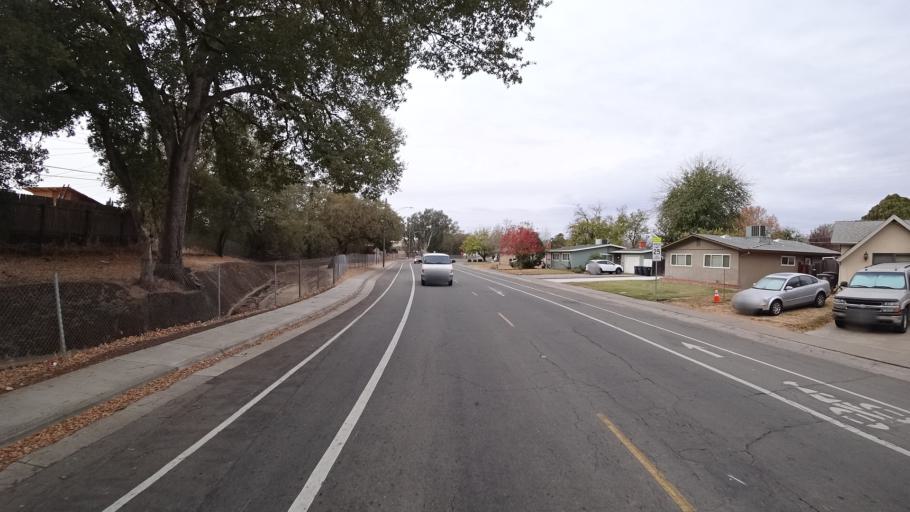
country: US
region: California
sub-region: Sacramento County
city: Citrus Heights
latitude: 38.7125
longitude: -121.2991
